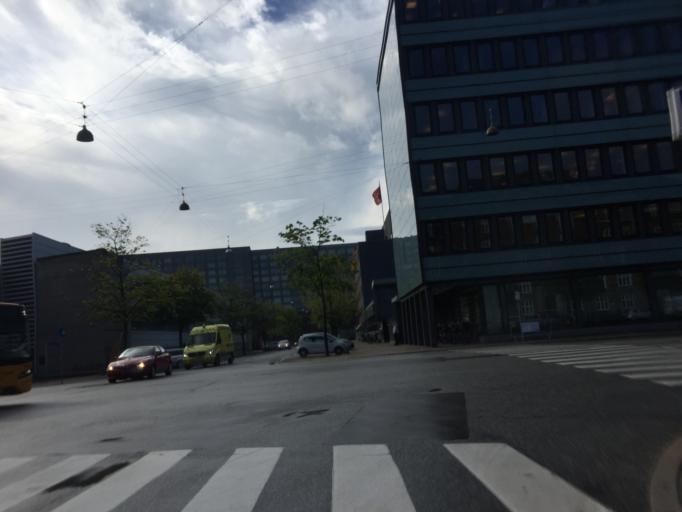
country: DK
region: Capital Region
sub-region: Kobenhavn
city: Copenhagen
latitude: 55.6703
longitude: 12.5710
